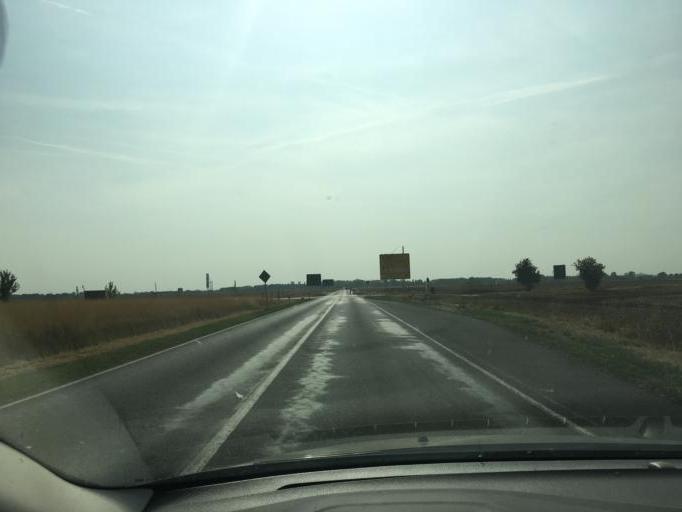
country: DE
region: Saxony-Anhalt
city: Barby
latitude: 51.9373
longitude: 11.8321
